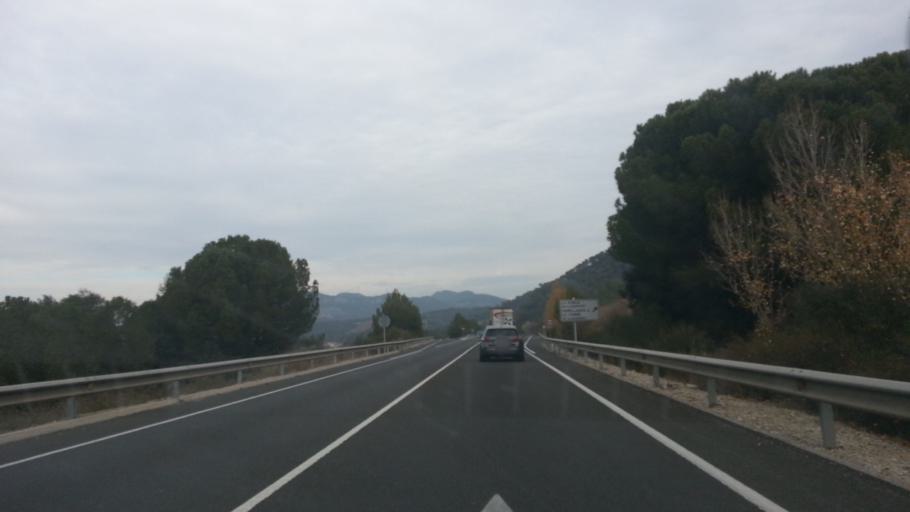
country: ES
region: Catalonia
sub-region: Provincia de Barcelona
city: Capellades
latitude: 41.5387
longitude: 1.6911
